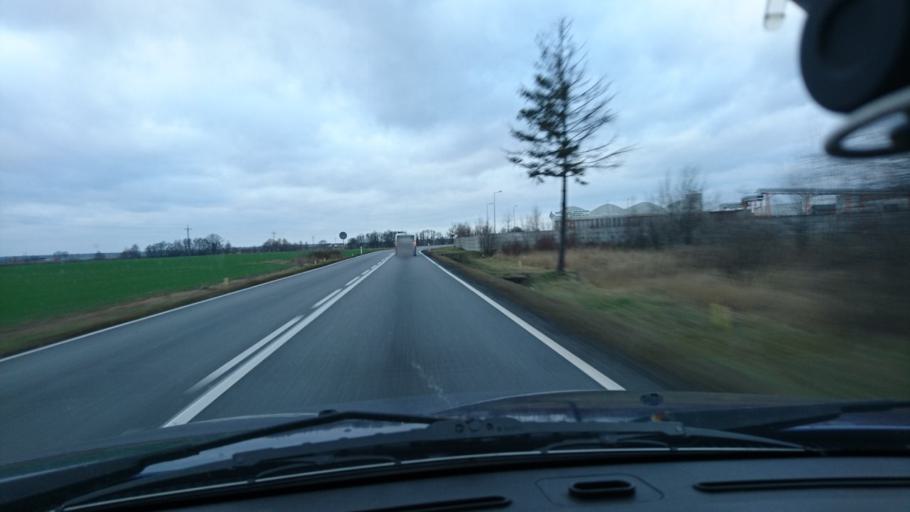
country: PL
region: Opole Voivodeship
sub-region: Powiat kluczborski
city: Kluczbork
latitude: 51.0012
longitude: 18.2057
